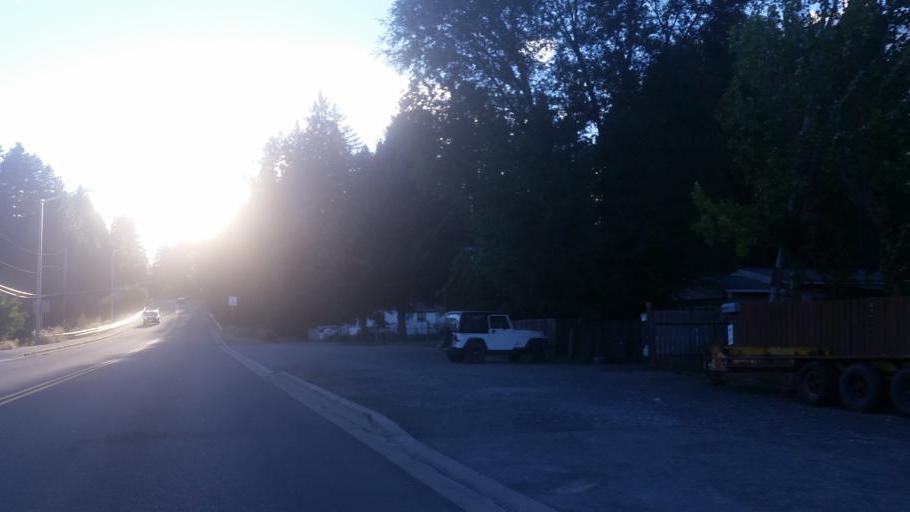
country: US
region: Washington
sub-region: Kittitas County
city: Cle Elum
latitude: 47.1958
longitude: -120.9454
